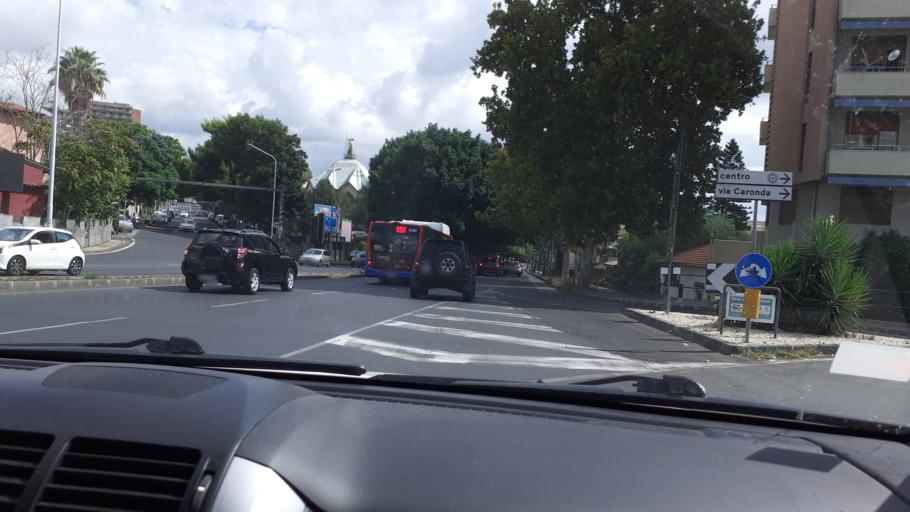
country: IT
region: Sicily
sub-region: Catania
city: Canalicchio
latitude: 37.5268
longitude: 15.0825
